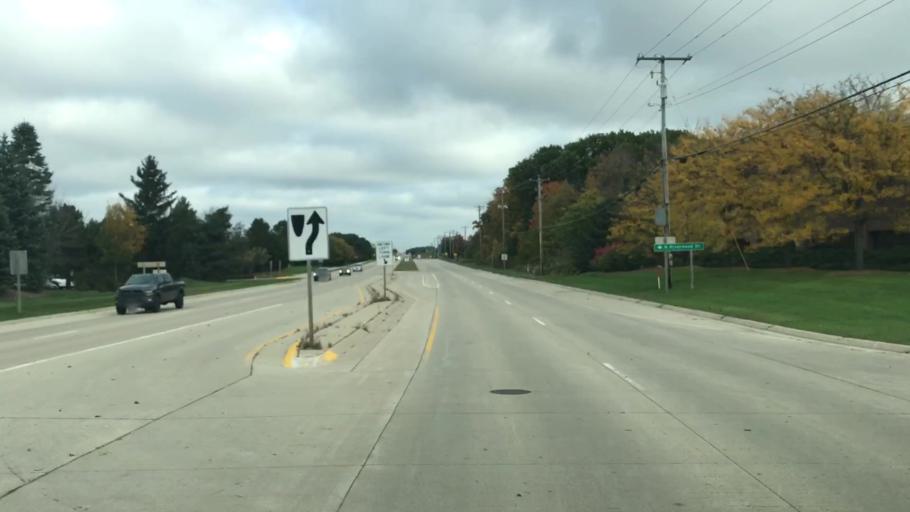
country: US
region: Wisconsin
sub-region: Waukesha County
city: Pewaukee
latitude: 43.0557
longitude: -88.2253
